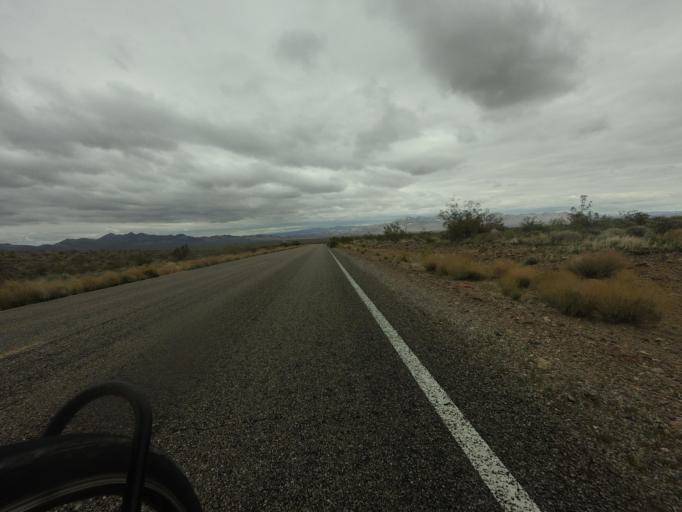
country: US
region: Nevada
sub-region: Nye County
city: Beatty
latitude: 36.8102
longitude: -116.9092
